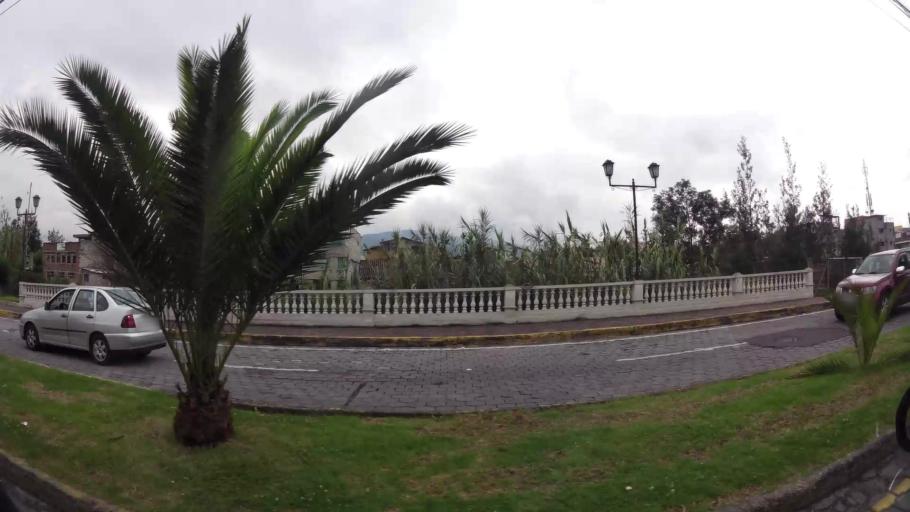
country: EC
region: Pichincha
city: Sangolqui
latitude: -0.3055
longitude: -78.4577
